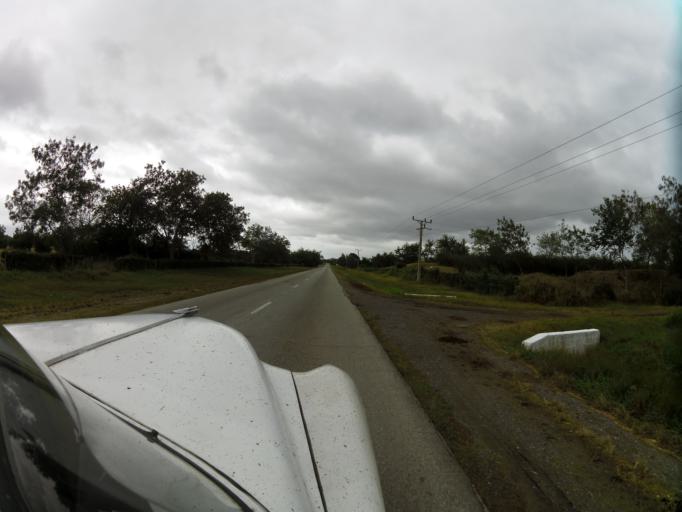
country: CU
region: Las Tunas
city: Las Tunas
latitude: 20.9223
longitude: -76.8947
